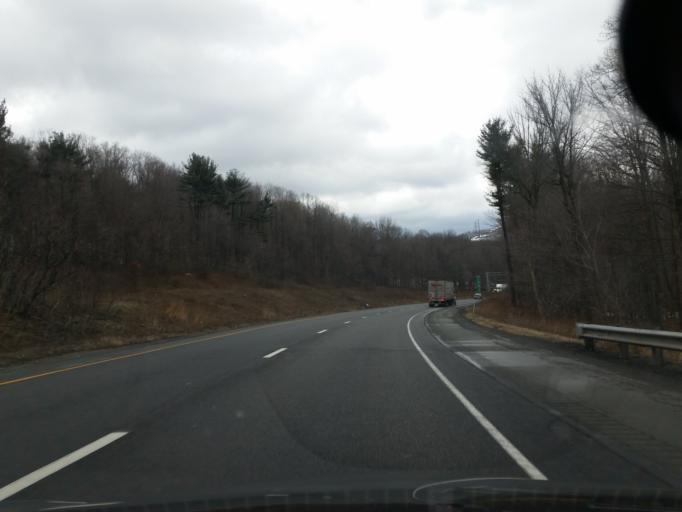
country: US
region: Pennsylvania
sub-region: Lackawanna County
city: Chinchilla
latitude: 41.4878
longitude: -75.6788
